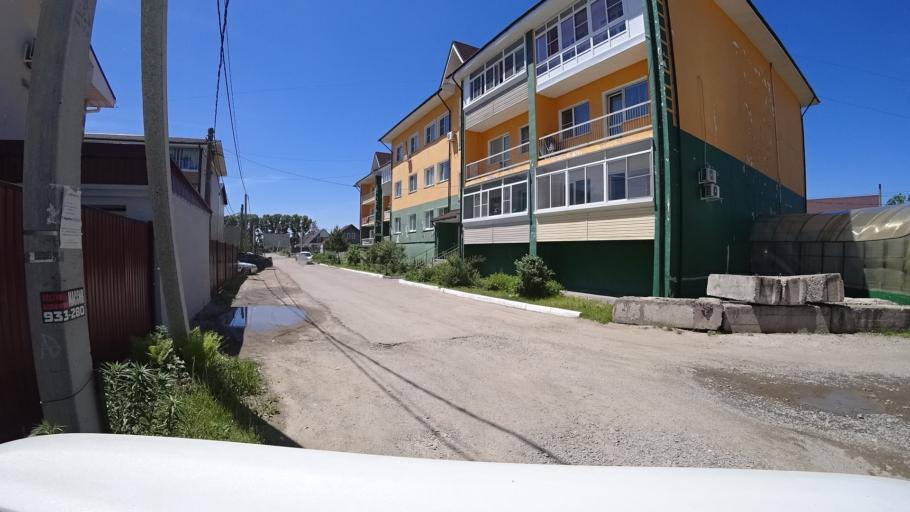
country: RU
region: Khabarovsk Krai
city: Topolevo
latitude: 48.5091
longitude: 135.1857
